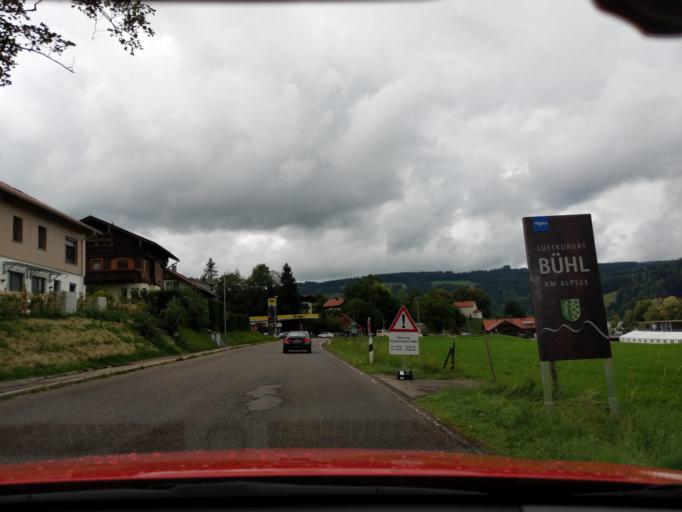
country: DE
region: Bavaria
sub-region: Swabia
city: Immenstadt im Allgau
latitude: 47.5661
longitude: 10.1941
